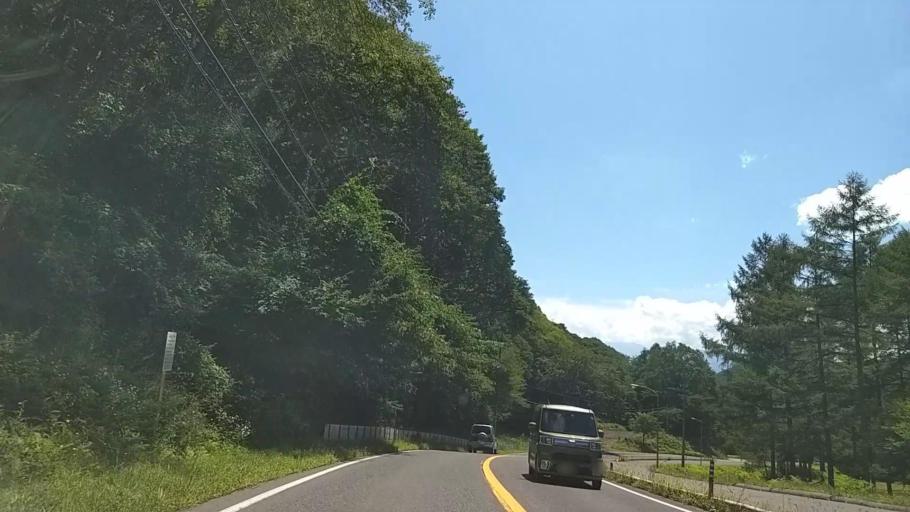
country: JP
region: Nagano
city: Chino
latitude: 36.0812
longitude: 138.2216
